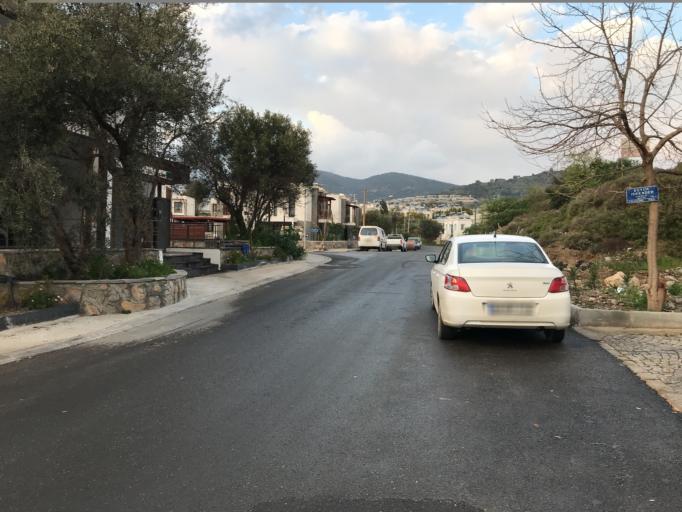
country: TR
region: Mugla
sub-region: Bodrum
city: Bodrum
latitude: 37.0352
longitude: 27.4100
